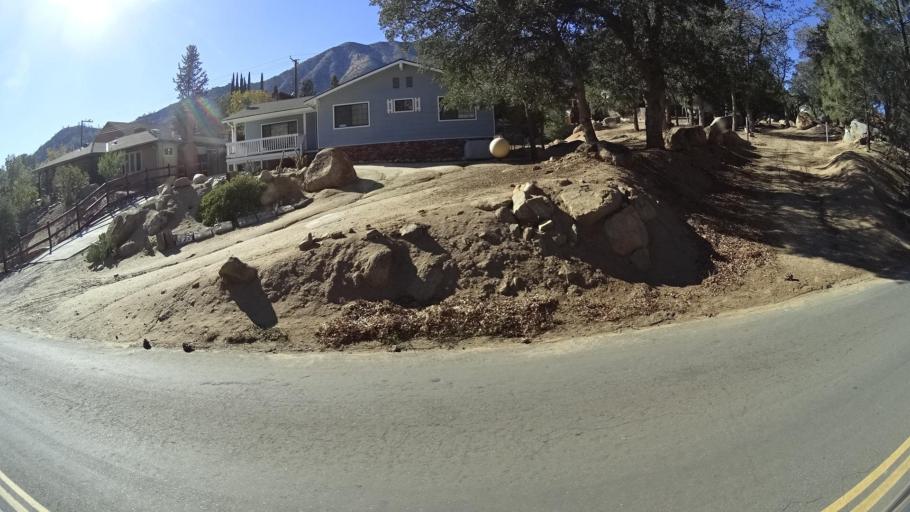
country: US
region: California
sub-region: Kern County
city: Kernville
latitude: 35.7652
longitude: -118.4321
